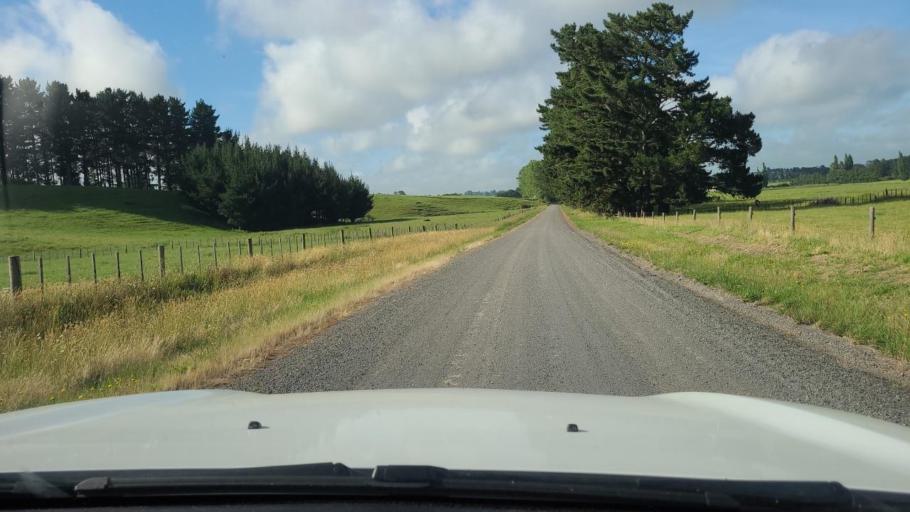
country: NZ
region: Bay of Plenty
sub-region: Western Bay of Plenty District
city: Katikati
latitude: -37.6081
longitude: 175.7971
